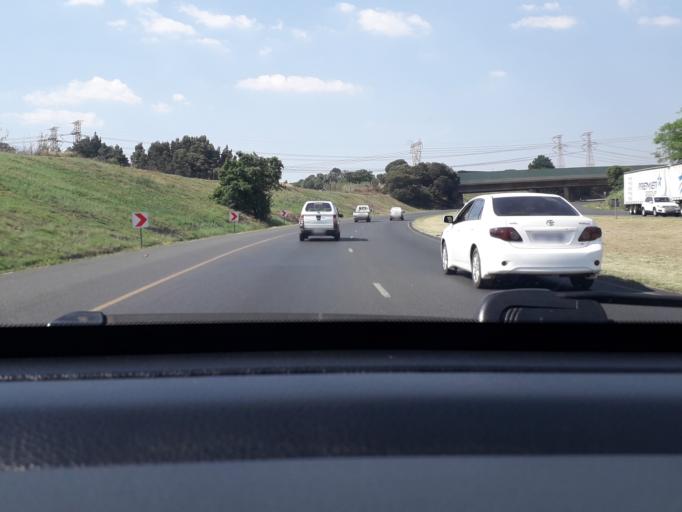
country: ZA
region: Gauteng
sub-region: City of Johannesburg Metropolitan Municipality
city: Modderfontein
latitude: -26.0920
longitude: 28.1858
